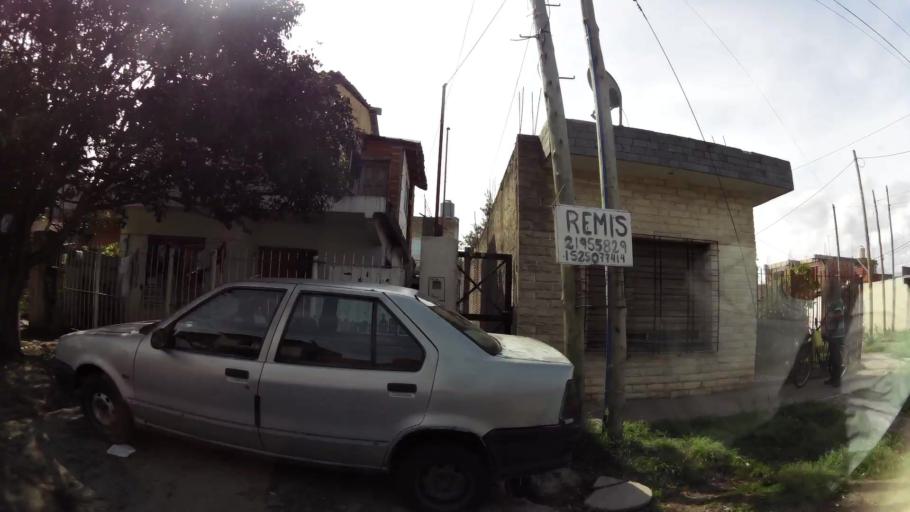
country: AR
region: Buenos Aires
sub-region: Partido de Quilmes
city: Quilmes
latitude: -34.7634
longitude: -58.2392
